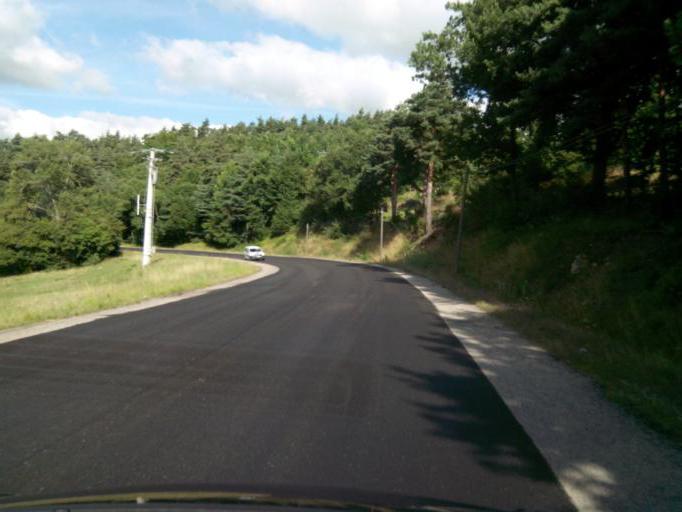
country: FR
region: Auvergne
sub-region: Departement de la Haute-Loire
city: Retournac
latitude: 45.2270
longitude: 4.0448
